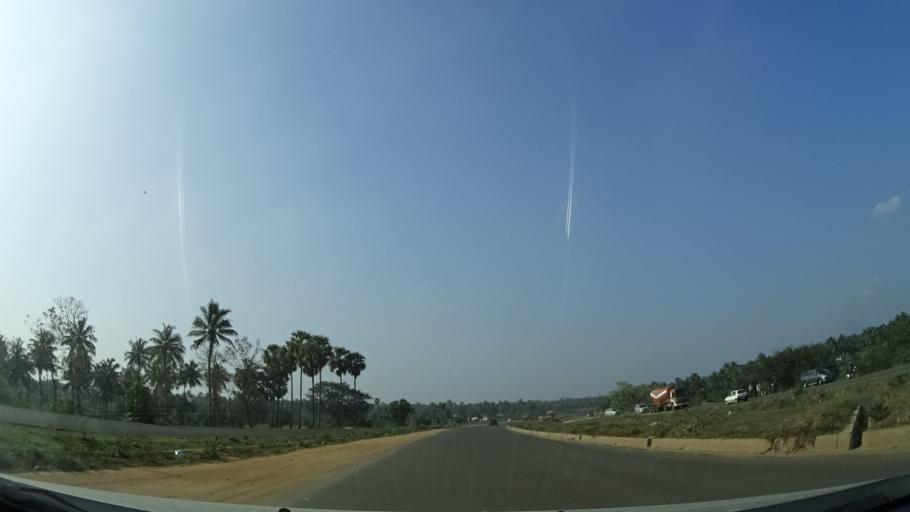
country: IN
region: Tamil Nadu
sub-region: Coimbatore
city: Madukkarai
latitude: 10.8760
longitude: 76.9057
